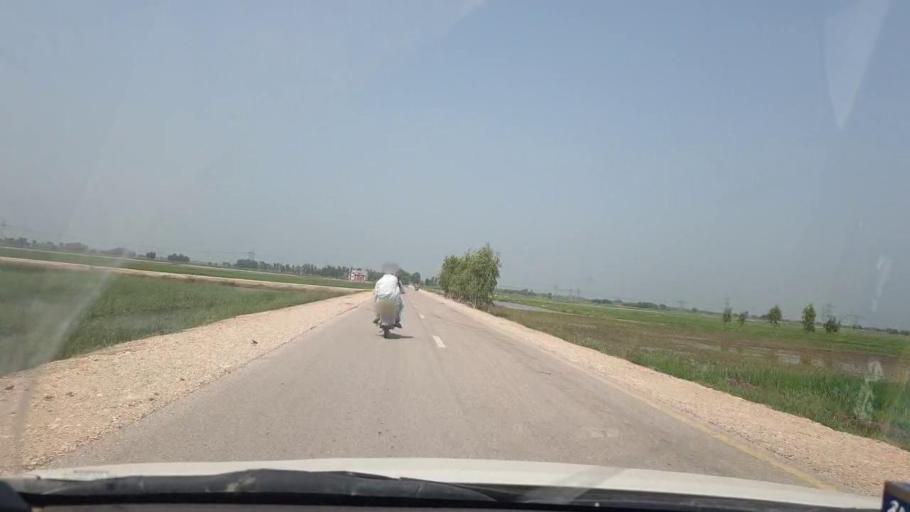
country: PK
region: Sindh
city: Rustam jo Goth
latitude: 27.9588
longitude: 68.7525
